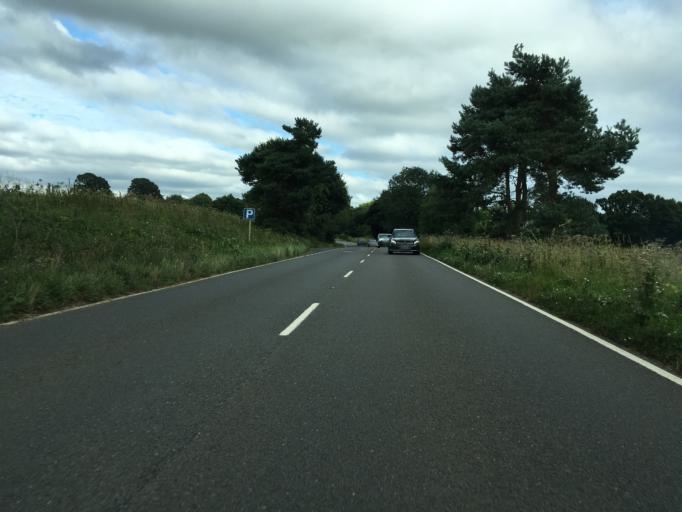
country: GB
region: England
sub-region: Hampshire
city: Liss
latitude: 51.0059
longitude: -0.8627
